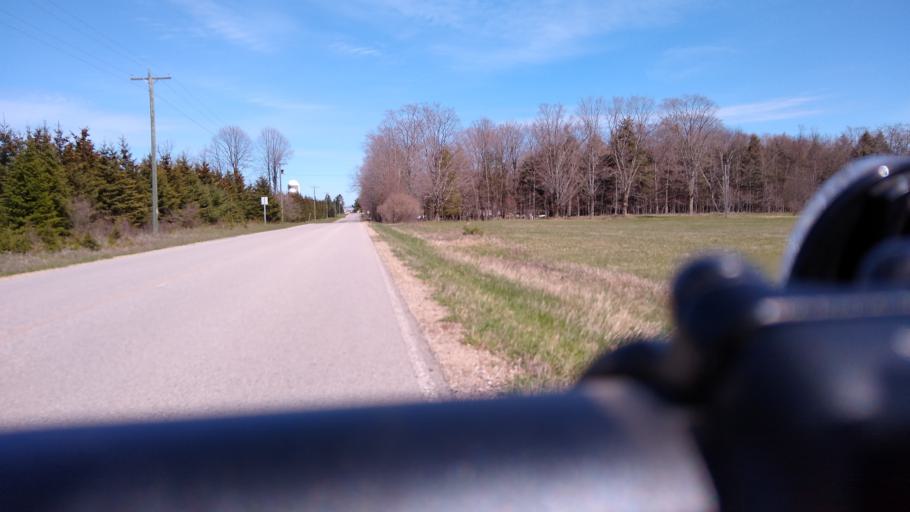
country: US
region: Michigan
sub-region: Delta County
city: Escanaba
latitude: 45.6955
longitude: -87.1597
